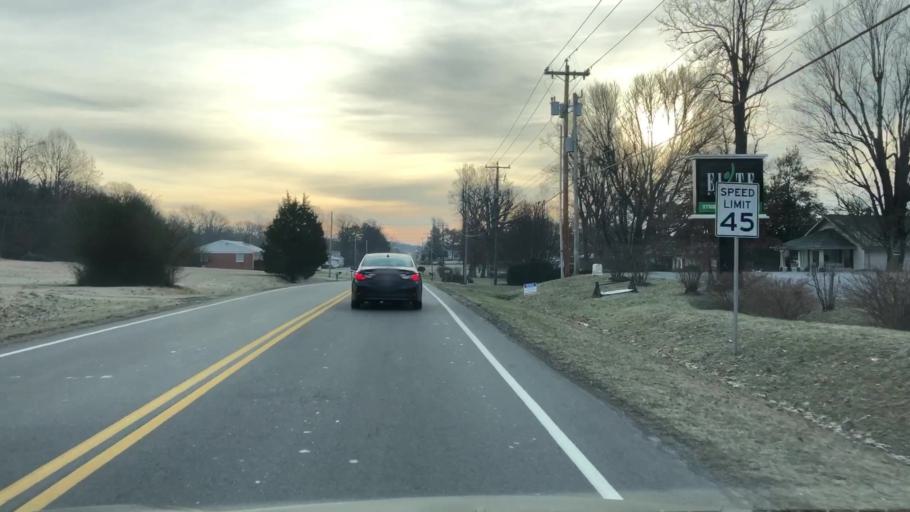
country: US
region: Virginia
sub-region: Campbell County
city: Timberlake
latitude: 37.3329
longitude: -79.2583
